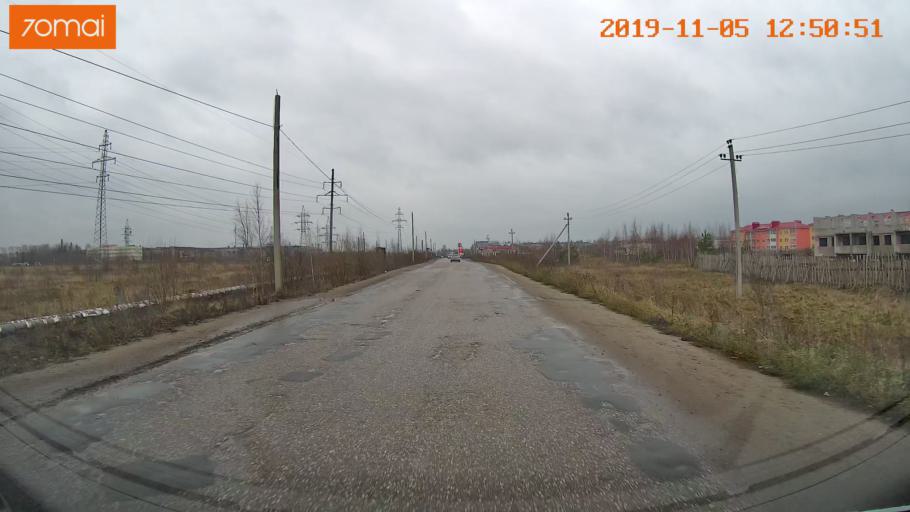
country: RU
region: Ivanovo
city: Kokhma
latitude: 56.9472
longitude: 41.1107
